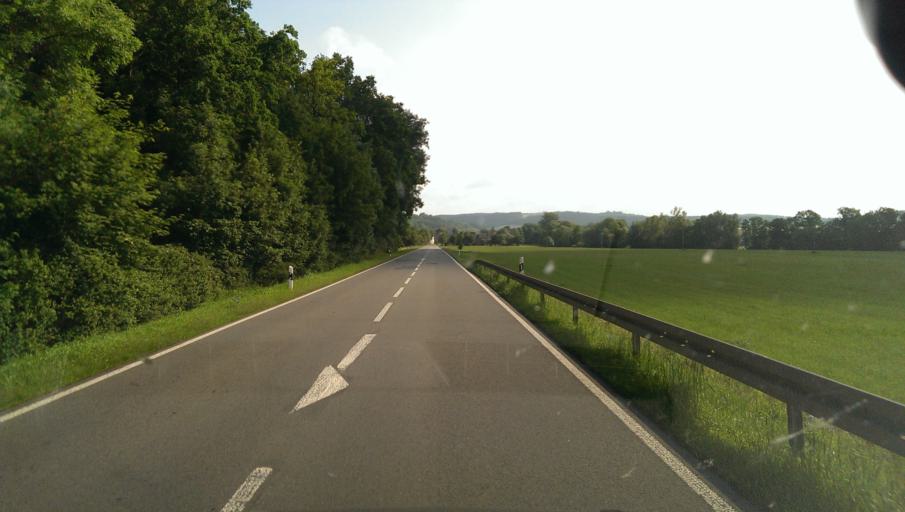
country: DE
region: Thuringia
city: Barchfeld
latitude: 50.7984
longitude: 11.1605
